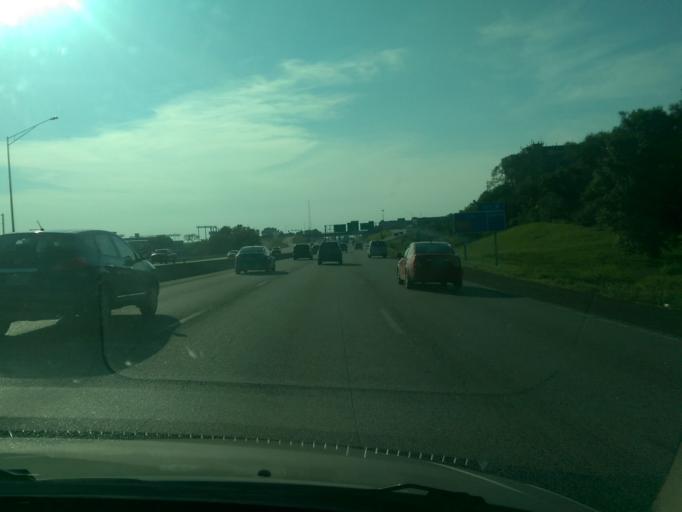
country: US
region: Missouri
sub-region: Jackson County
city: Raytown
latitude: 39.0491
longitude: -94.4683
